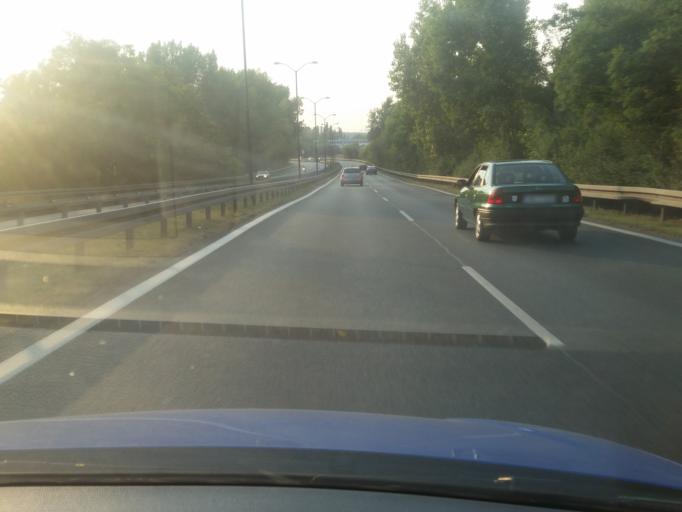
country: PL
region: Silesian Voivodeship
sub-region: Katowice
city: Katowice
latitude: 50.2608
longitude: 19.0645
